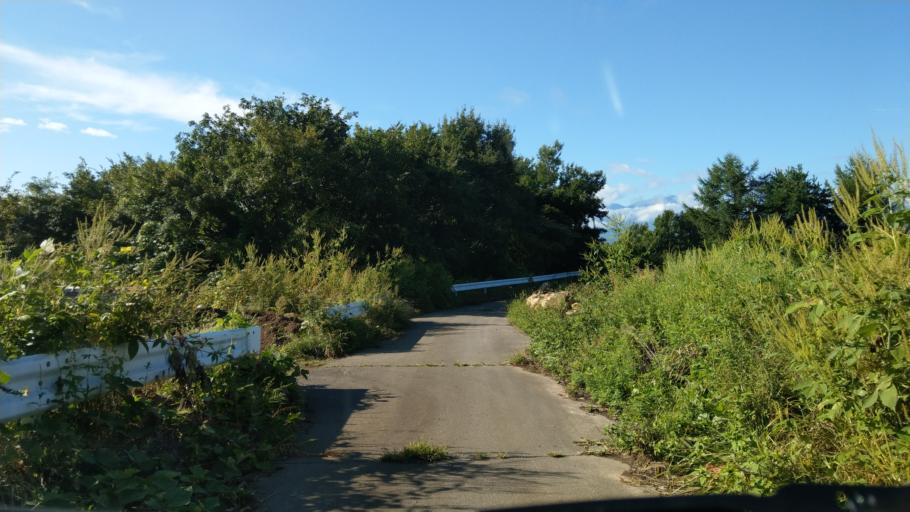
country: JP
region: Nagano
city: Komoro
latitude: 36.3431
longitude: 138.4344
